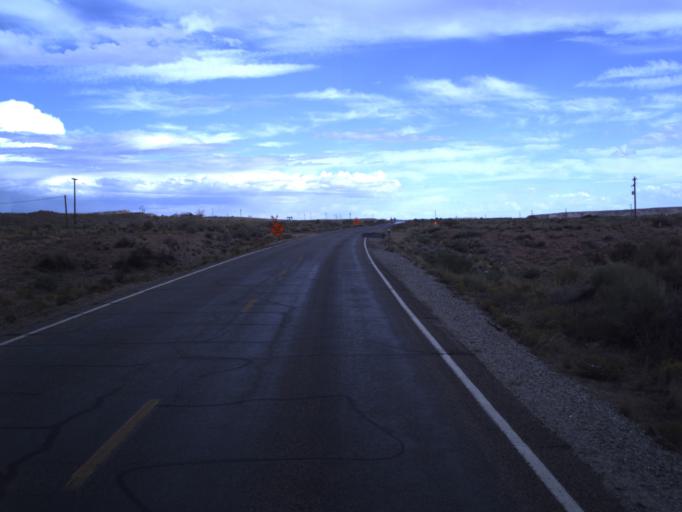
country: US
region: Utah
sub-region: San Juan County
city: Blanding
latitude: 37.2331
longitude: -109.2191
